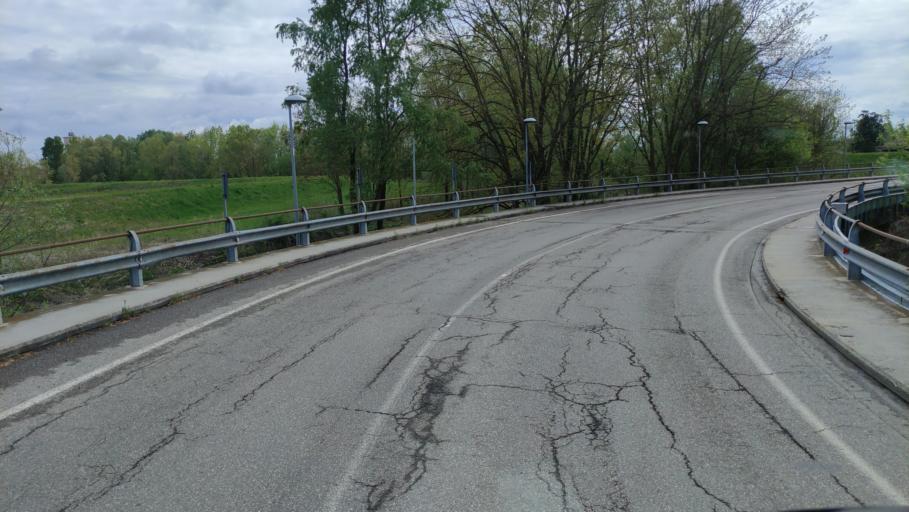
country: IT
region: Emilia-Romagna
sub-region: Provincia di Parma
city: Colorno
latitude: 44.9316
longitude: 10.3718
